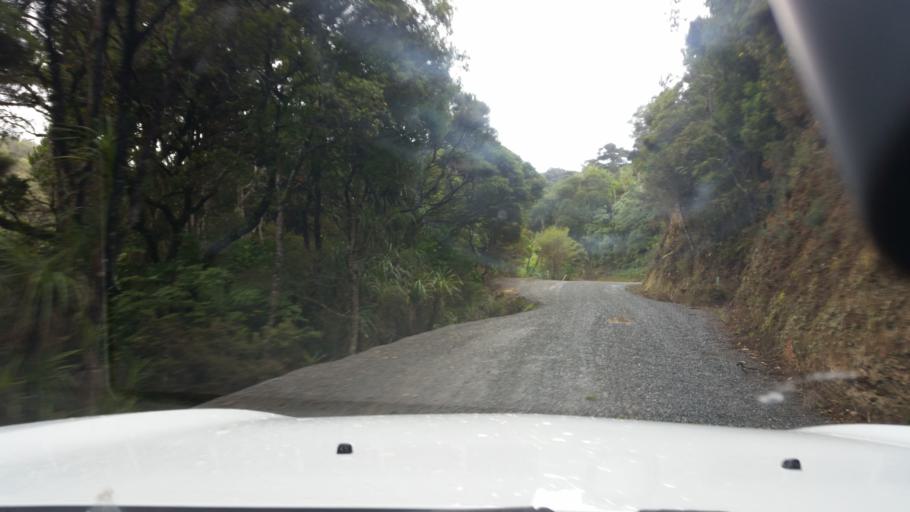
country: NZ
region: Northland
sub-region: Whangarei
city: Ruakaka
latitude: -35.7752
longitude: 174.5397
